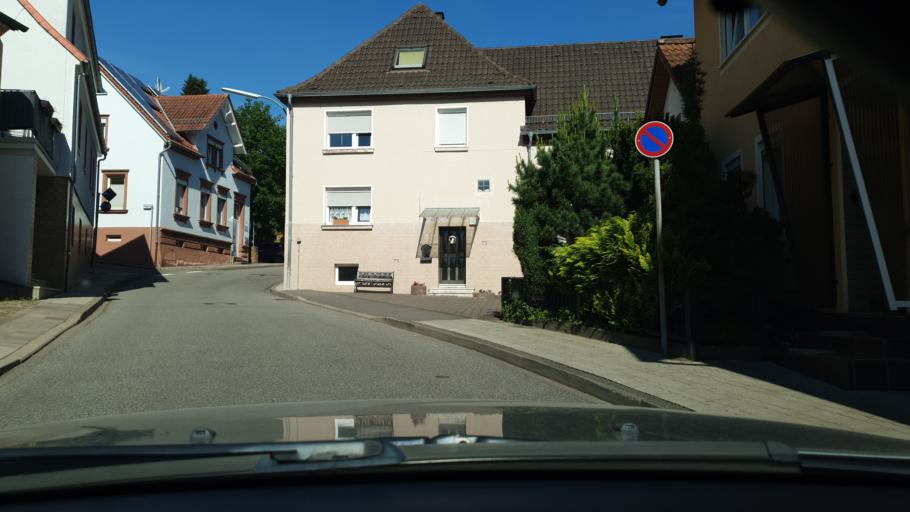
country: DE
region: Rheinland-Pfalz
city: Otterberg
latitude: 49.4785
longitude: 7.7770
